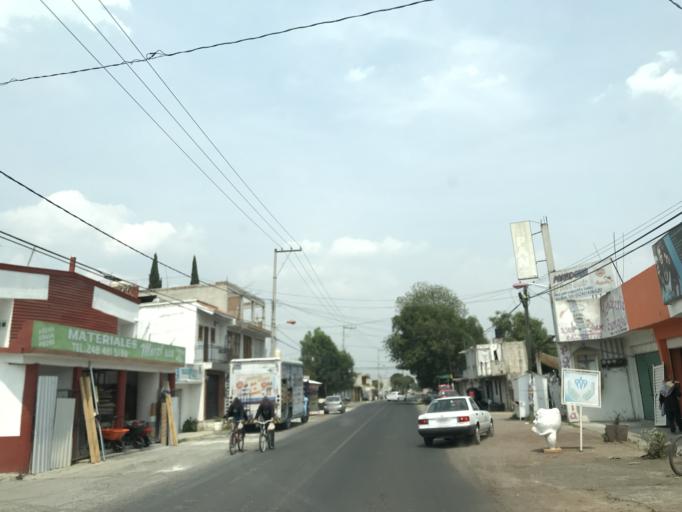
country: MX
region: Tlaxcala
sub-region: Ixtacuixtla de Mariano Matamoros
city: Santa Justina Ecatepec
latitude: 19.3080
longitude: -98.3729
